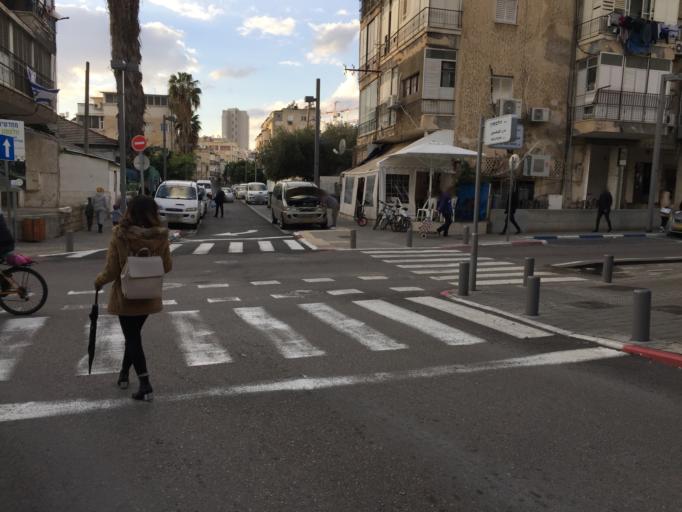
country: IL
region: Tel Aviv
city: Tel Aviv
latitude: 32.0561
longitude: 34.7781
